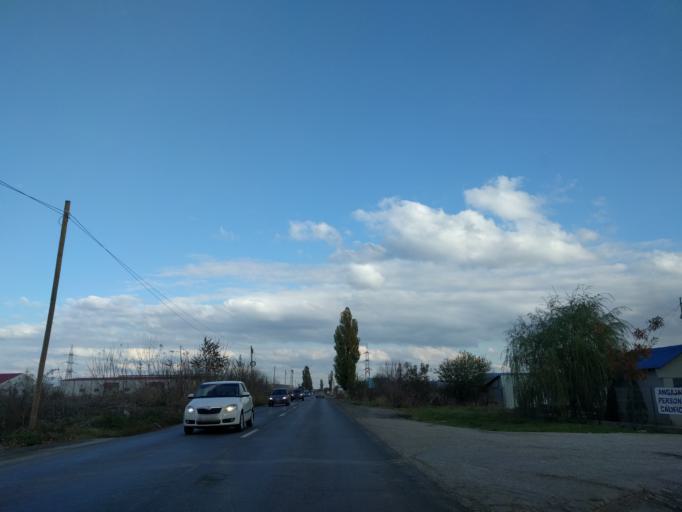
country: RO
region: Ilfov
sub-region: Comuna Cernica
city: Caldararu
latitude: 44.4520
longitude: 26.2468
